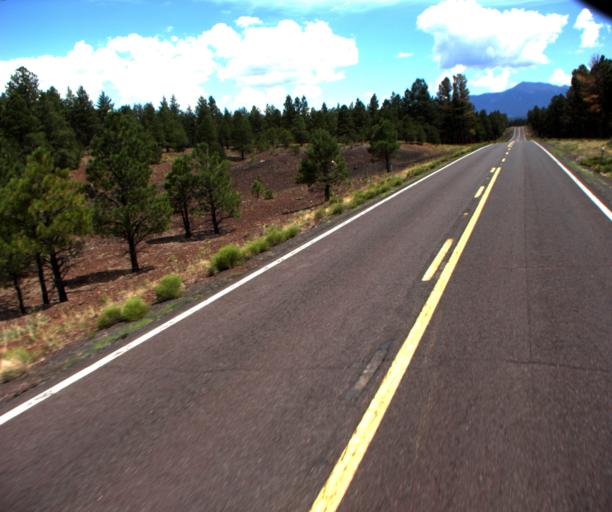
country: US
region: Arizona
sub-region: Coconino County
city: Parks
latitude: 35.4952
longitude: -111.8145
